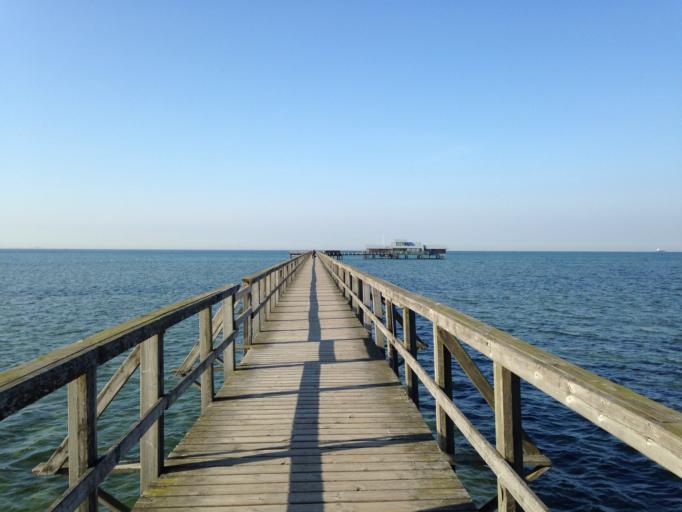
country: SE
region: Skane
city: Bjarred
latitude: 55.7099
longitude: 13.0224
